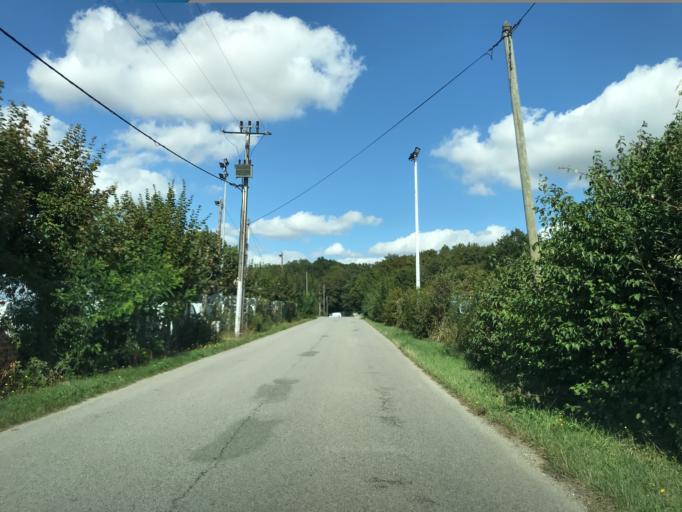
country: FR
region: Haute-Normandie
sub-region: Departement de l'Eure
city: La Chapelle-Reanville
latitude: 49.0936
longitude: 1.3920
